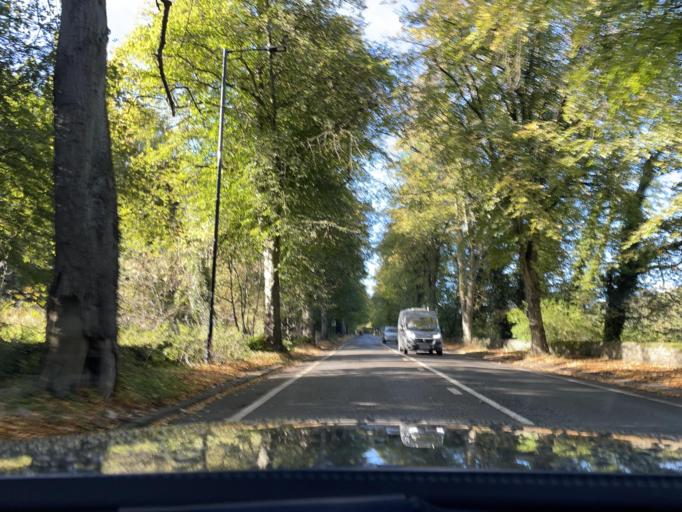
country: GB
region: England
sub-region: Sheffield
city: Oughtibridge
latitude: 53.3903
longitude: -1.5186
